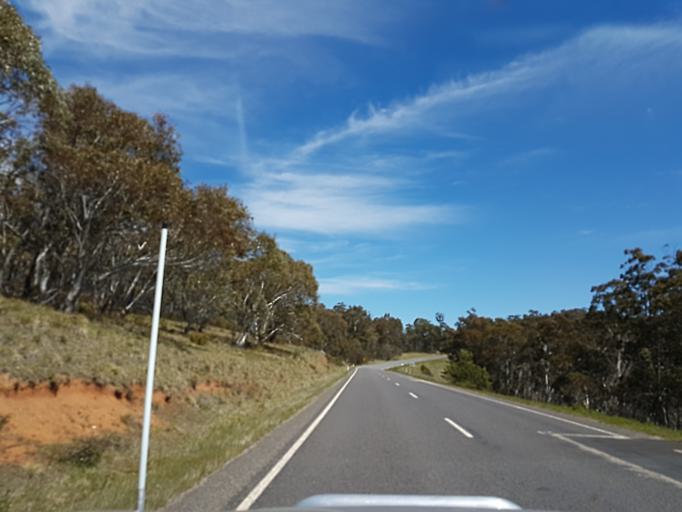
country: AU
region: Victoria
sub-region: Alpine
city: Mount Beauty
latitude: -37.0815
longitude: 147.3648
